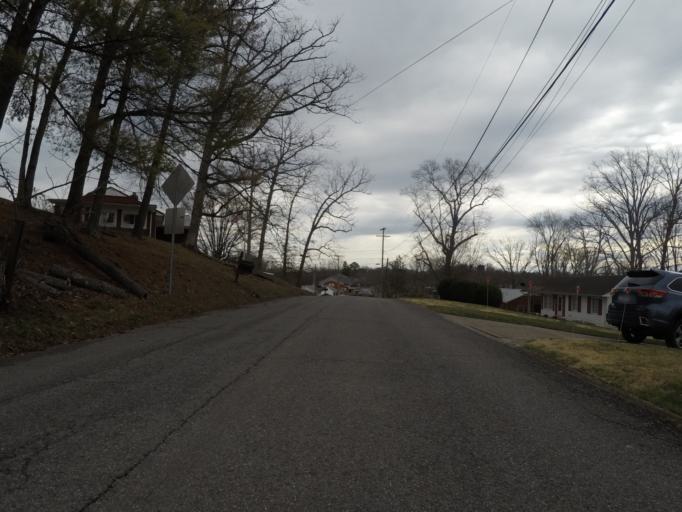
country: US
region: West Virginia
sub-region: Cabell County
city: Pea Ridge
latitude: 38.3953
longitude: -82.3816
